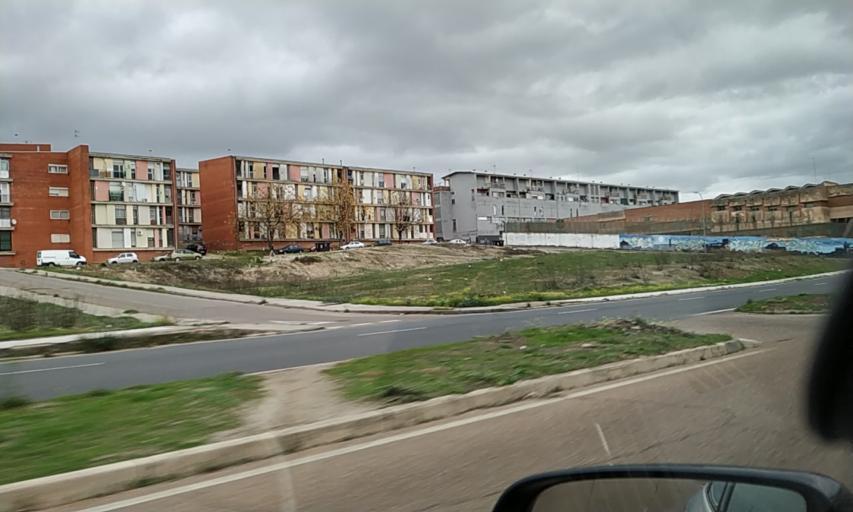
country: ES
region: Extremadura
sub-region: Provincia de Badajoz
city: Badajoz
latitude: 38.8974
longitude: -6.9856
